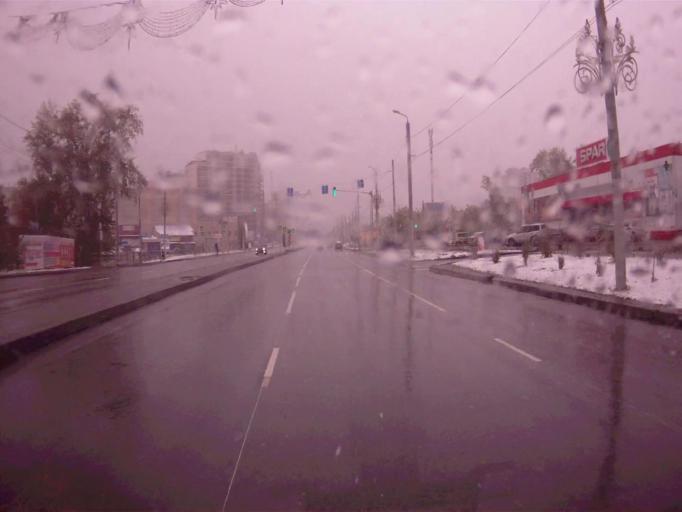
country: RU
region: Chelyabinsk
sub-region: Gorod Chelyabinsk
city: Chelyabinsk
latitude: 55.1439
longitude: 61.4055
